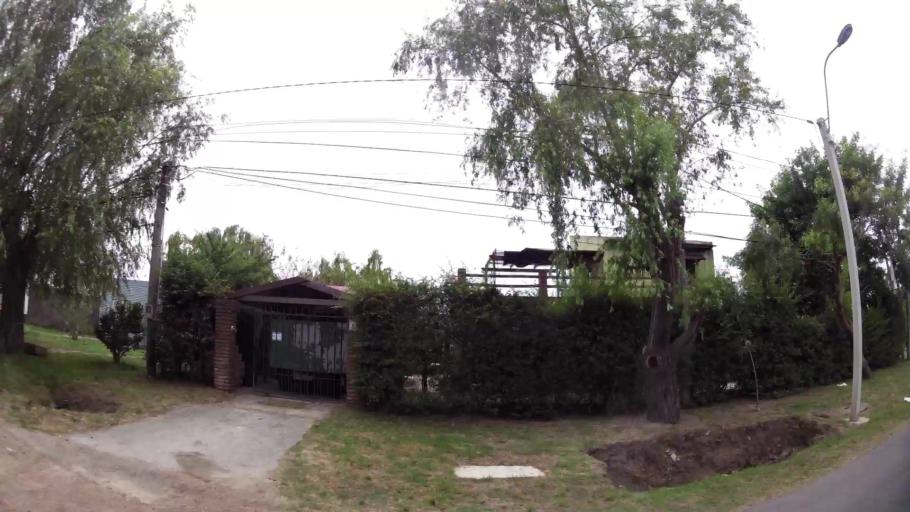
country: UY
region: Canelones
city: La Paz
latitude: -34.7572
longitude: -56.2258
